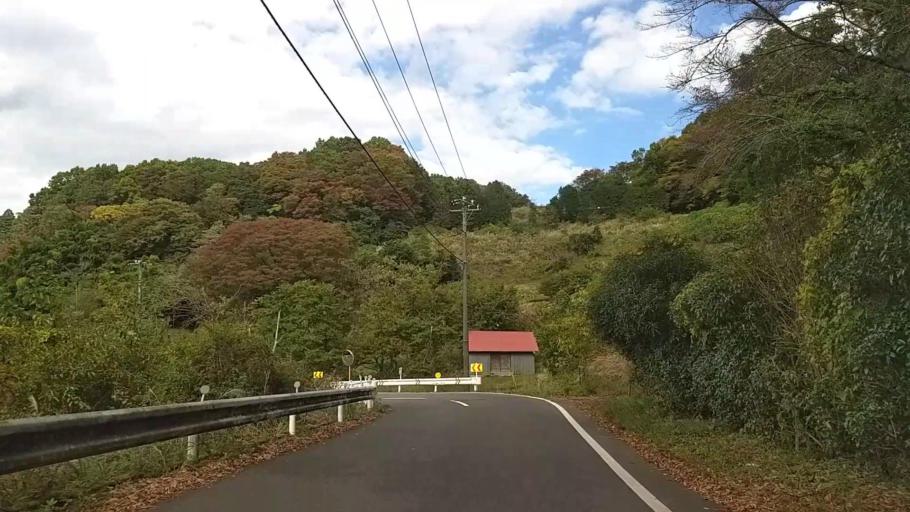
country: JP
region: Kanagawa
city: Hadano
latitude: 35.3538
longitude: 139.1708
